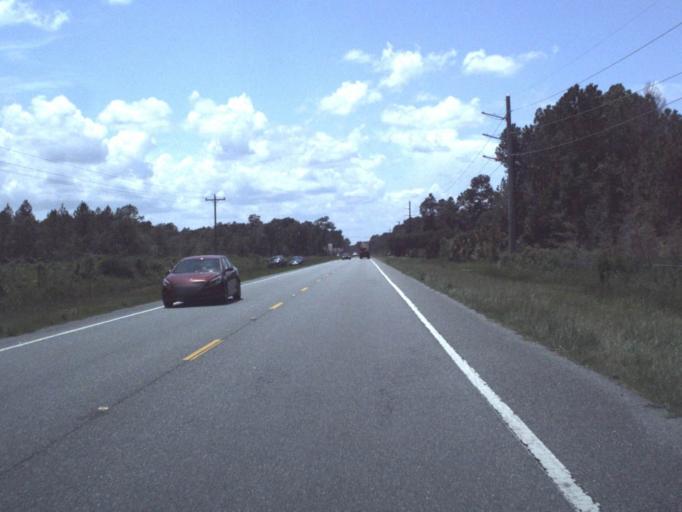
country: US
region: Florida
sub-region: Bradford County
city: Starke
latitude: 29.9592
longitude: -82.1624
